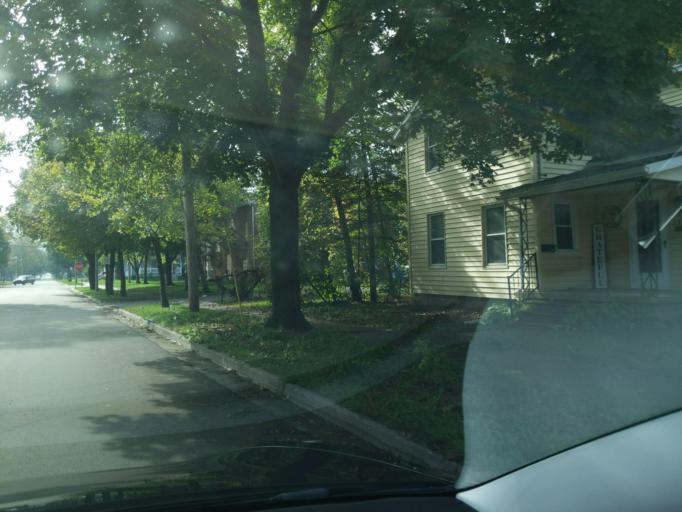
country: US
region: Michigan
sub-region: Eaton County
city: Charlotte
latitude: 42.5631
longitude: -84.8385
